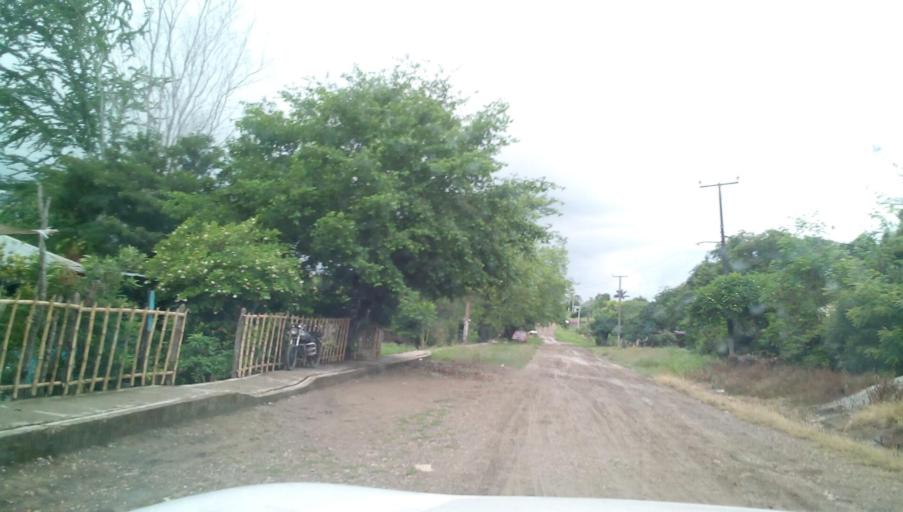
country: MX
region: Veracruz
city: Panuco
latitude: 21.8011
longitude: -98.1034
